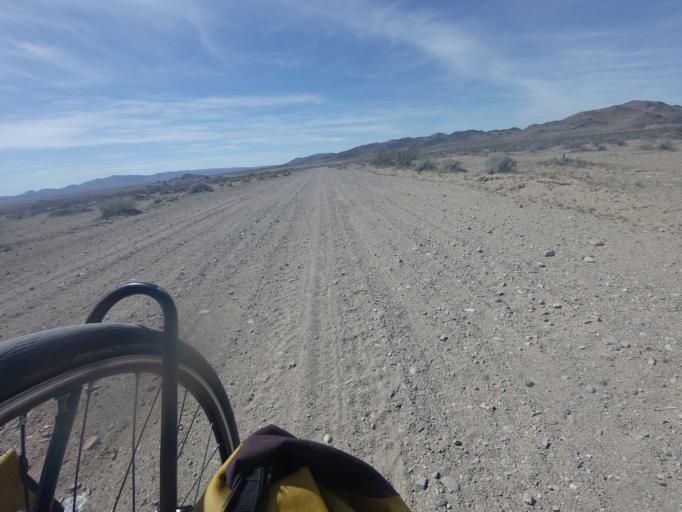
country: US
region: California
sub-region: San Bernardino County
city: Searles Valley
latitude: 35.5976
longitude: -117.3989
